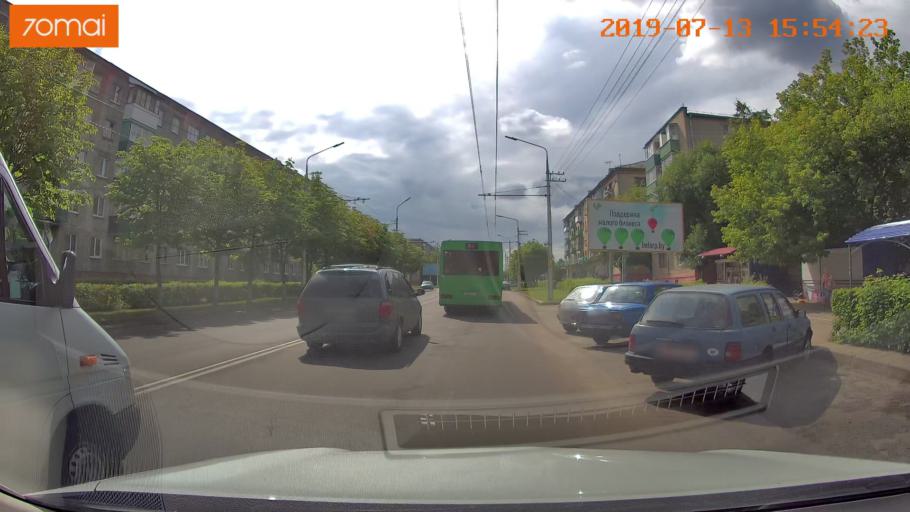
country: BY
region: Mogilev
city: Babruysk
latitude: 53.1385
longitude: 29.2018
